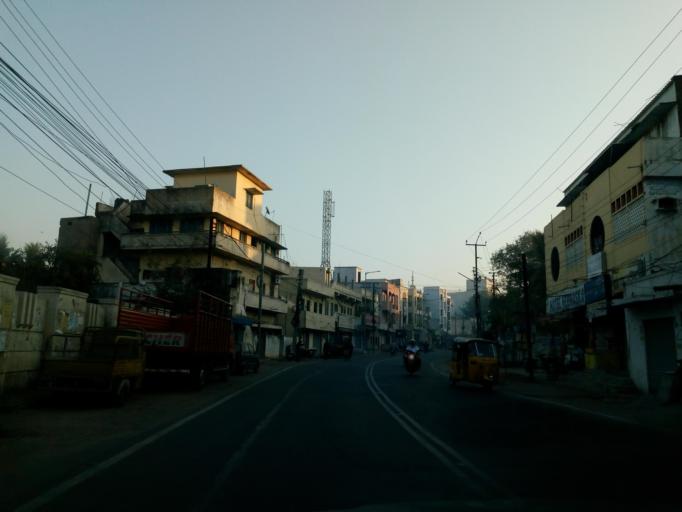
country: IN
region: Telangana
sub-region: Hyderabad
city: Malkajgiri
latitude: 17.4077
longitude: 78.5135
